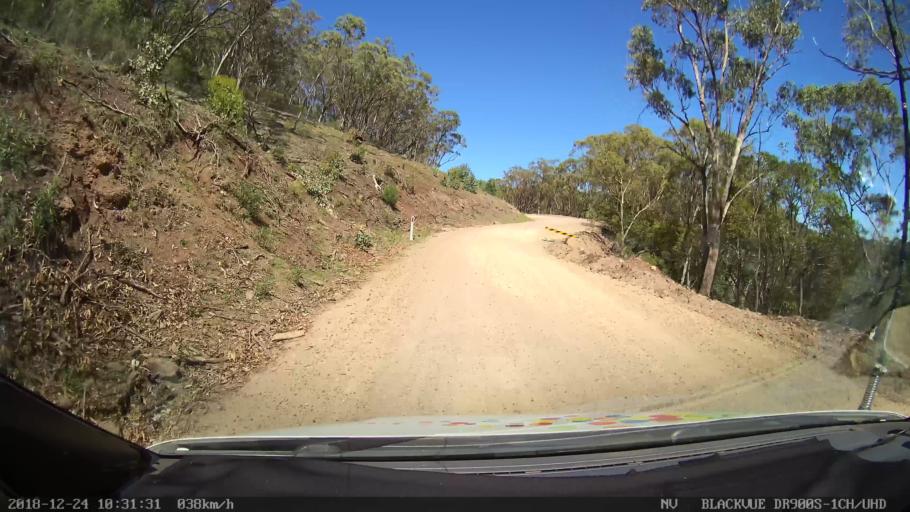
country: AU
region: New South Wales
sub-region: Upper Hunter Shire
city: Merriwa
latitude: -31.8392
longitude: 150.5215
